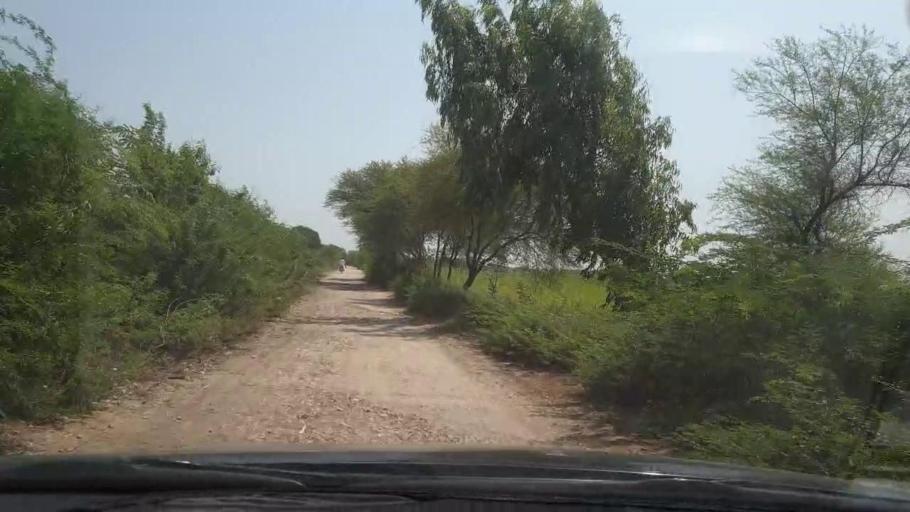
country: PK
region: Sindh
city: Tando Bago
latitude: 24.7726
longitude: 69.1905
